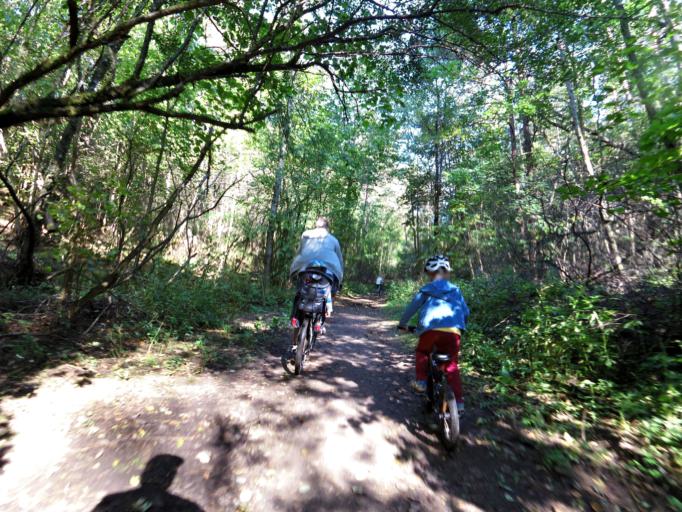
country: LT
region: Vilnius County
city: Pilaite
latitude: 54.6928
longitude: 25.1982
